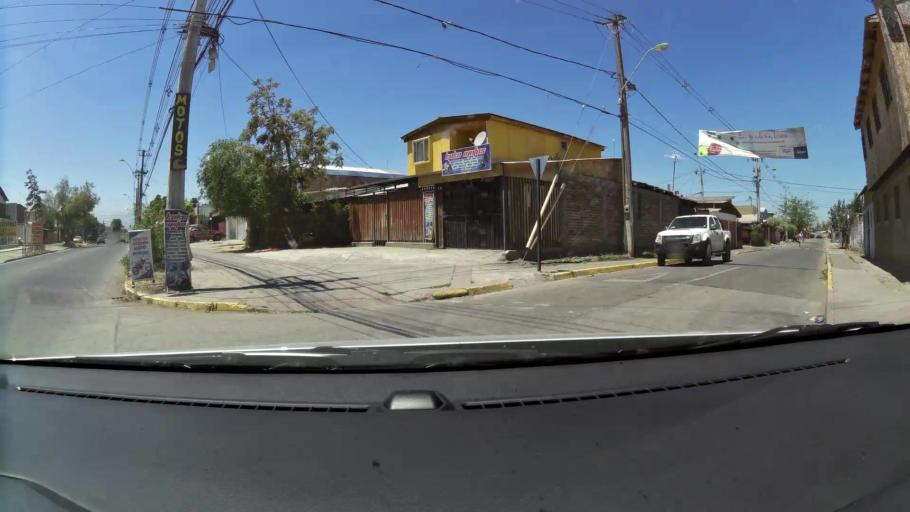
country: CL
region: Santiago Metropolitan
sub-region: Provincia de Maipo
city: San Bernardo
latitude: -33.5721
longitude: -70.6697
